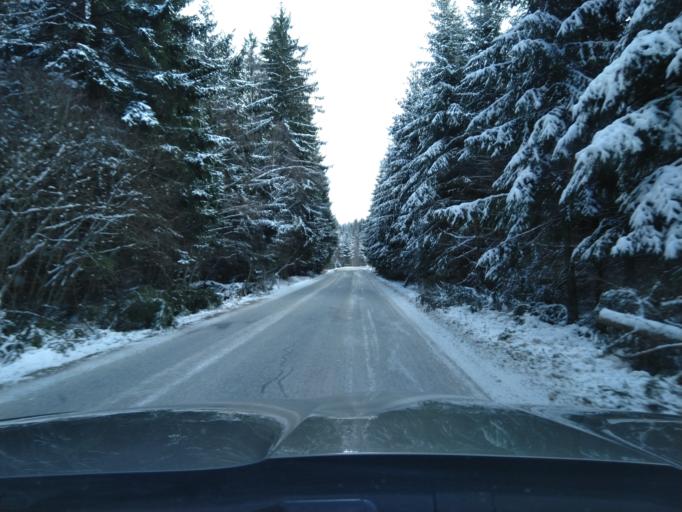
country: CZ
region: Jihocesky
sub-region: Okres Prachatice
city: Zdikov
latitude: 49.0484
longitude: 13.6665
